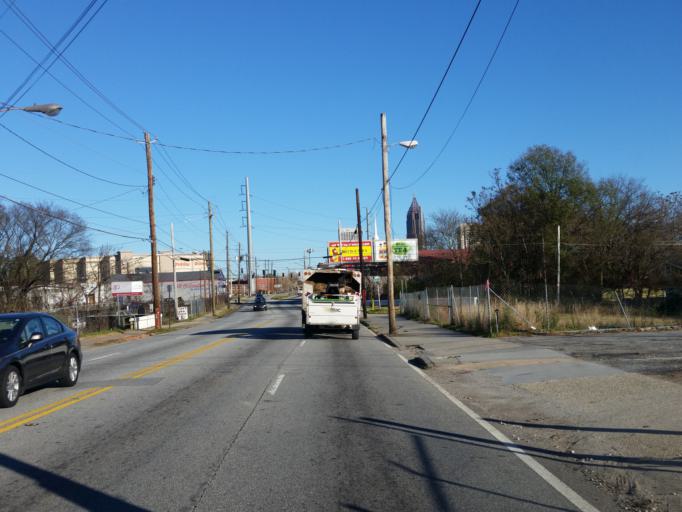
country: US
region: Georgia
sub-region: Fulton County
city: Atlanta
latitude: 33.7731
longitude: -84.4112
